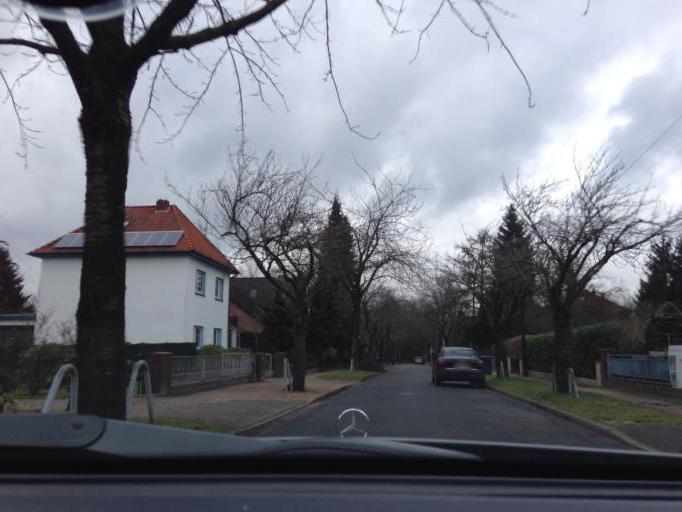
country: DE
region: Hamburg
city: Farmsen-Berne
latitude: 53.5862
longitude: 10.1144
